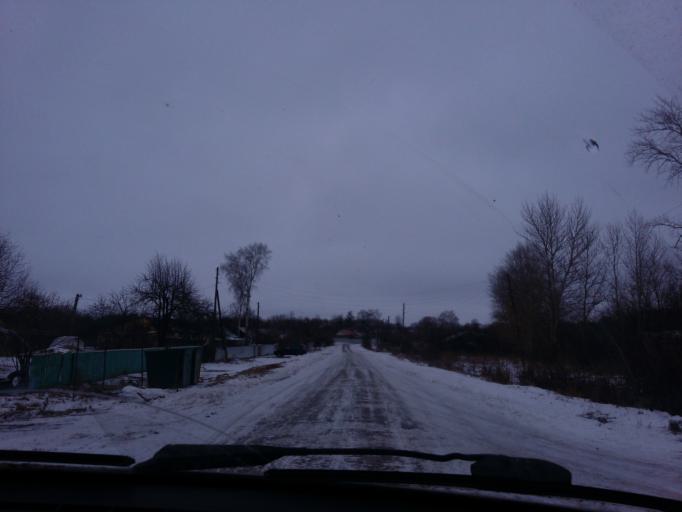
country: RU
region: Tula
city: Plavsk
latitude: 53.8134
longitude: 37.3861
